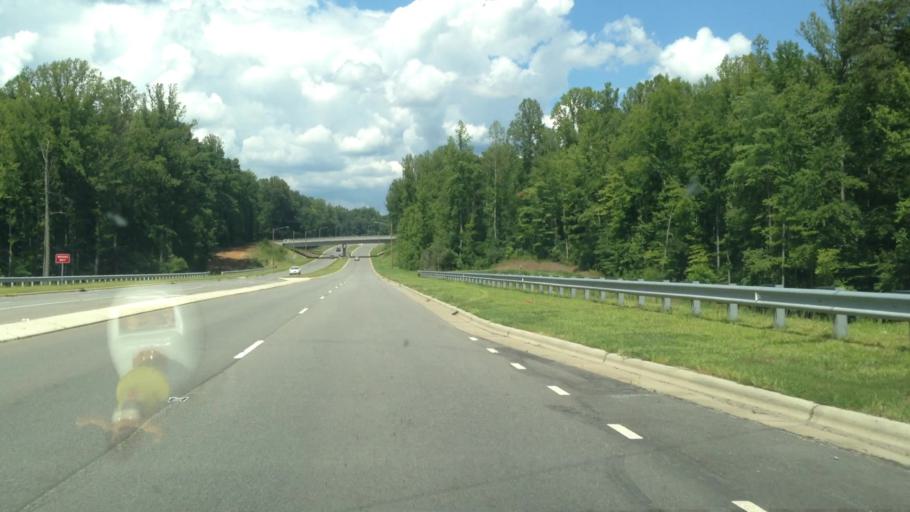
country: US
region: North Carolina
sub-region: Rockingham County
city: Reidsville
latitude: 36.3678
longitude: -79.6797
